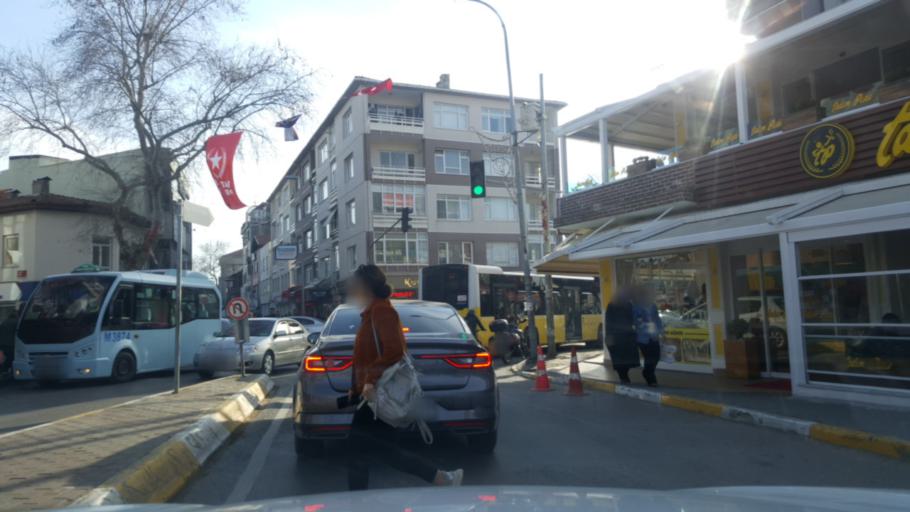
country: TR
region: Istanbul
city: Icmeler
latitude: 40.8177
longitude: 29.3045
